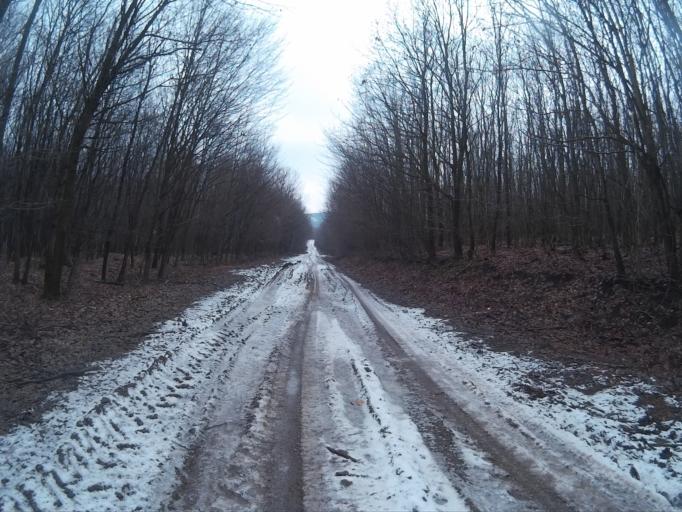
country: HU
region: Komarom-Esztergom
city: Tarjan
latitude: 47.5848
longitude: 18.5250
